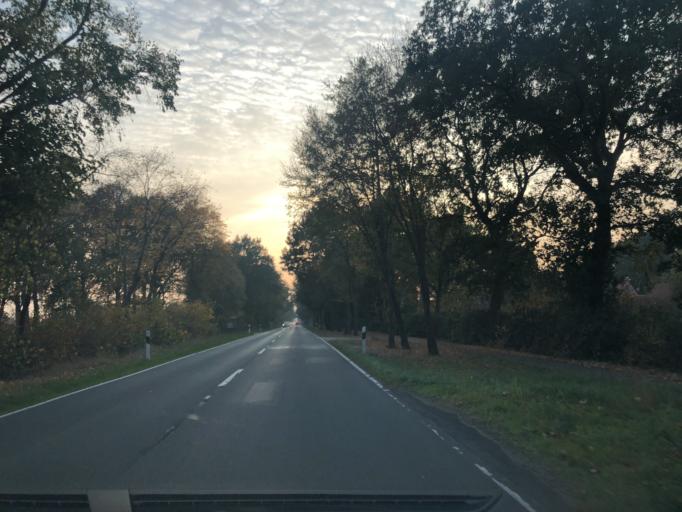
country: DE
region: Lower Saxony
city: Wardenburg
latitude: 53.0407
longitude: 8.1162
